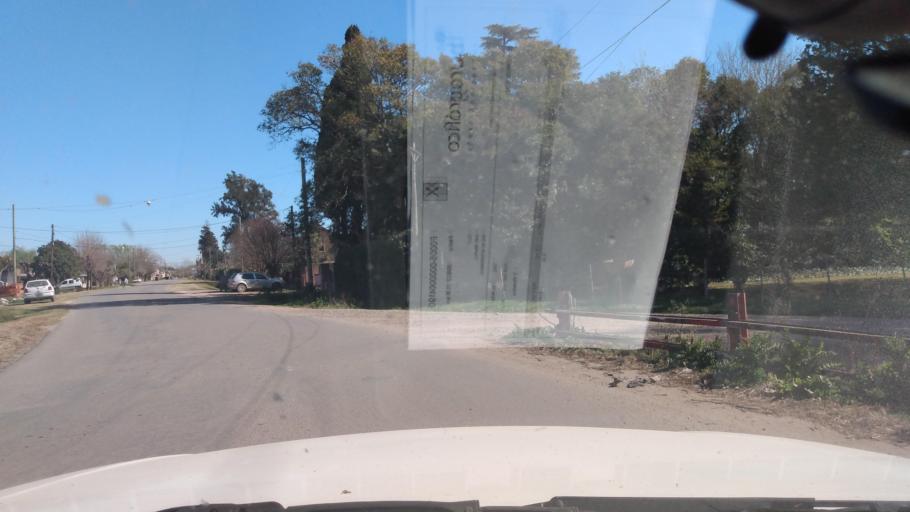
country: AR
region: Buenos Aires
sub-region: Partido de Mercedes
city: Mercedes
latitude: -34.6583
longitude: -59.4051
